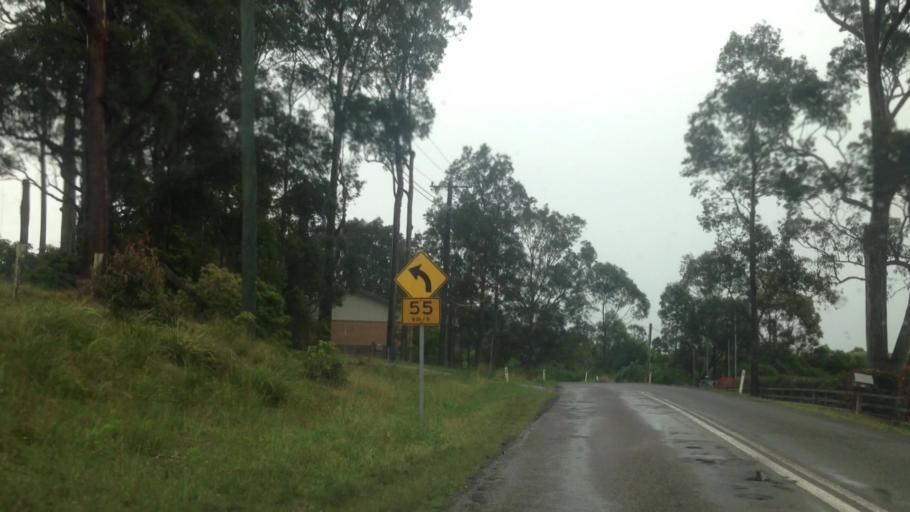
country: AU
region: New South Wales
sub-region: Wyong Shire
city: Little Jilliby
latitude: -33.2407
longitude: 151.3813
